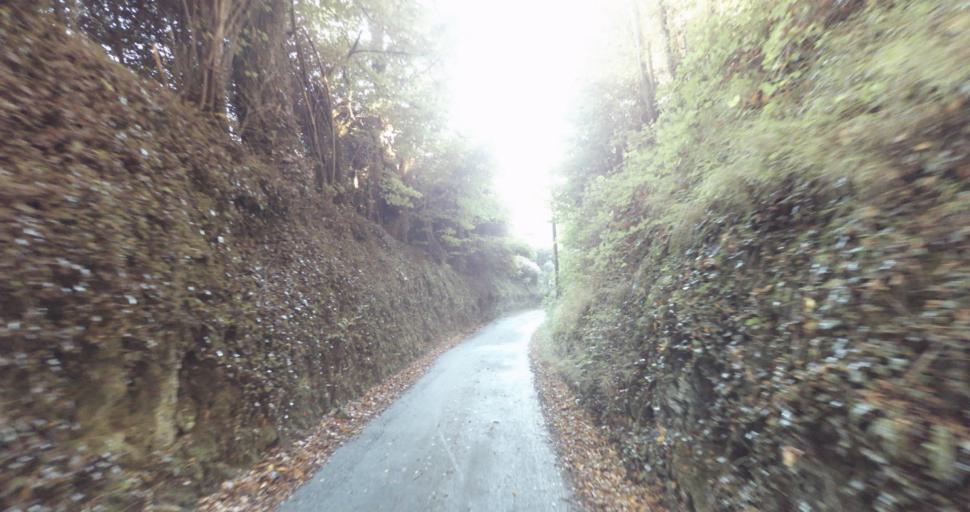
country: FR
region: Lower Normandy
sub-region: Departement de l'Orne
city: Vimoutiers
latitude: 48.9211
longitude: 0.1736
